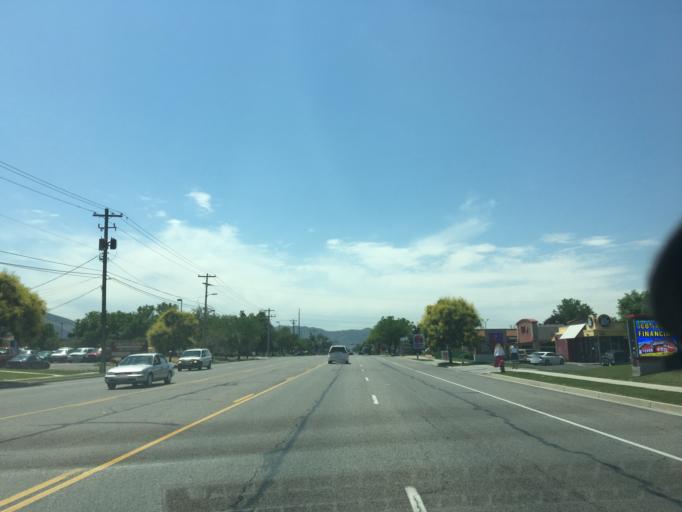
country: US
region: Utah
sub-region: Salt Lake County
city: Sandy City
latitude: 40.5835
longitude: -111.8723
